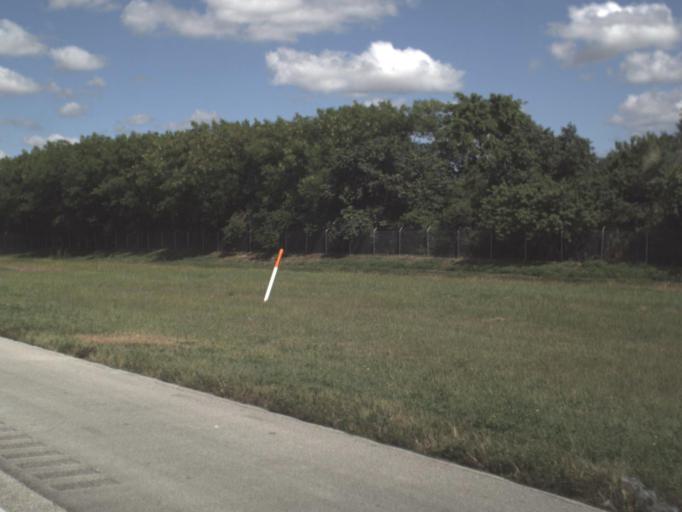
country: US
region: Florida
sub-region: Broward County
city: Coral Springs
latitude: 26.2927
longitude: -80.2970
